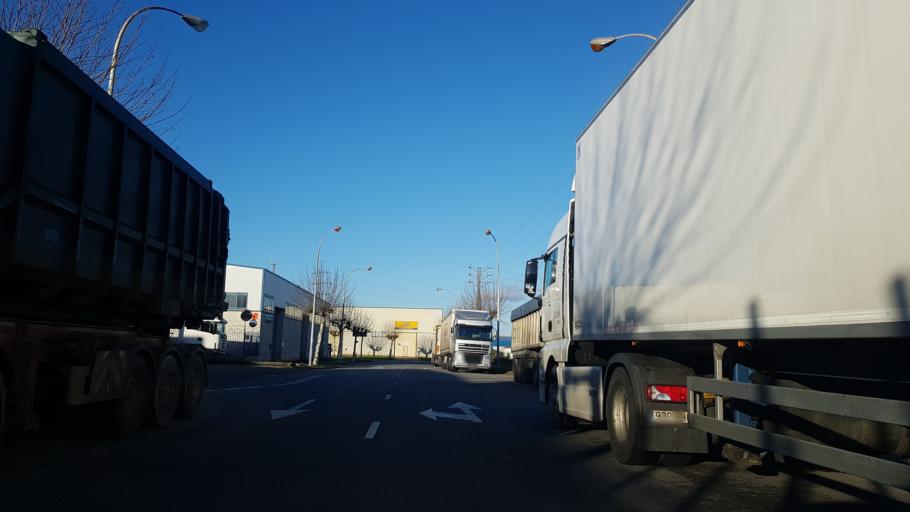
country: ES
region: Galicia
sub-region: Provincia de Lugo
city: Lugo
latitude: 43.0459
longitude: -7.5611
